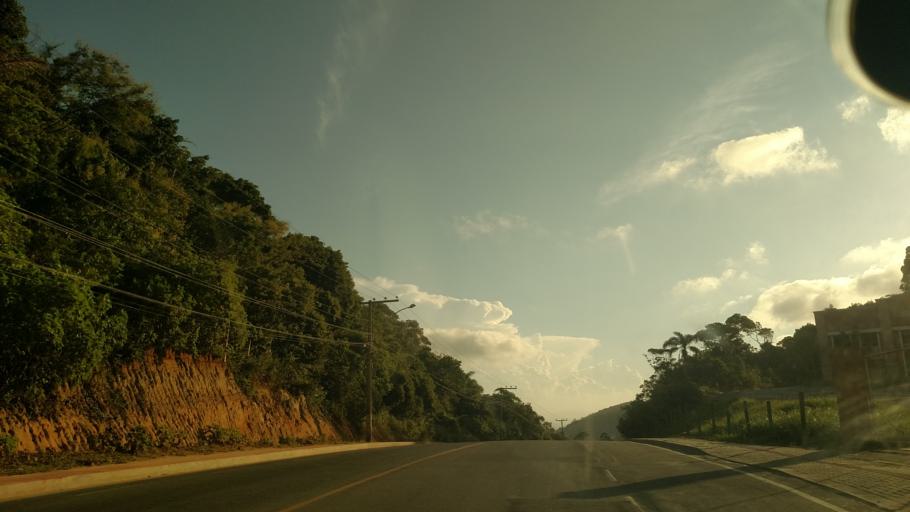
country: BR
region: Santa Catarina
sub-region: Porto Belo
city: Porto Belo
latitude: -27.1594
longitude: -48.5162
